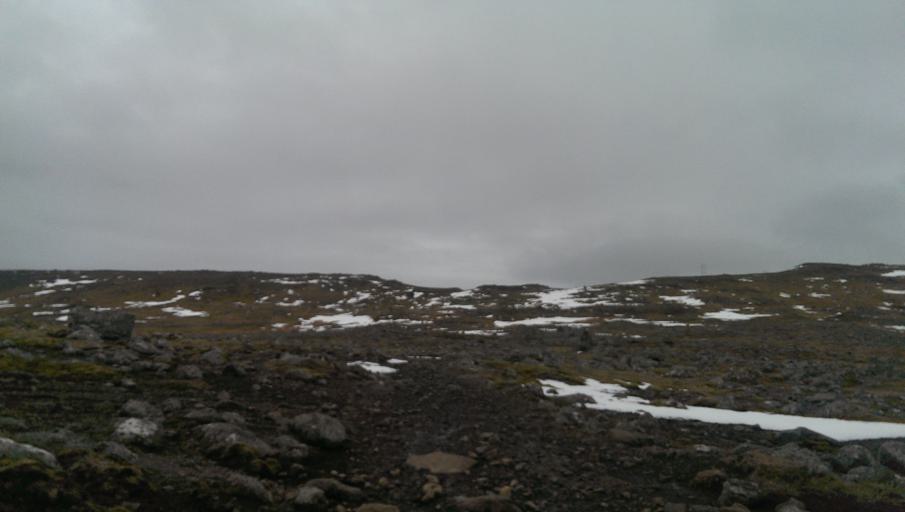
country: FO
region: Streymoy
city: Kollafjordhur
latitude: 62.0309
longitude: -6.8763
